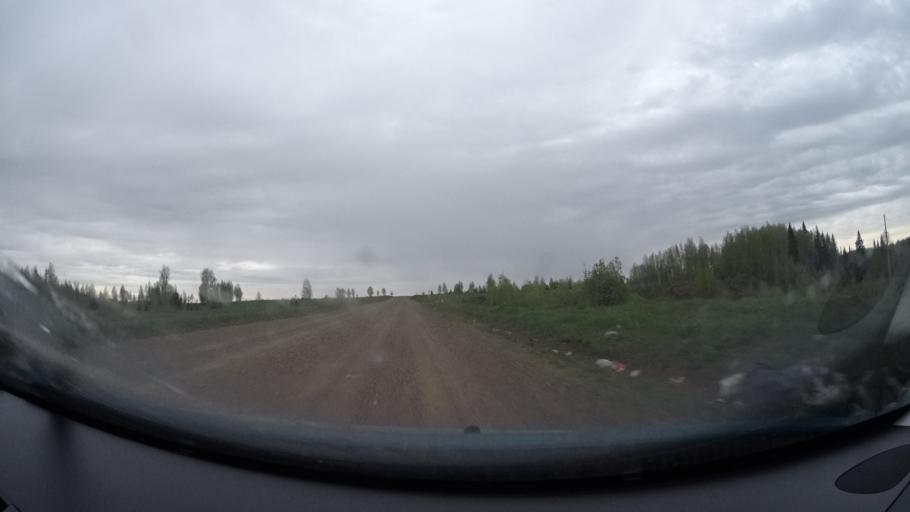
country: RU
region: Perm
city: Kuyeda
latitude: 56.5739
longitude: 55.6830
